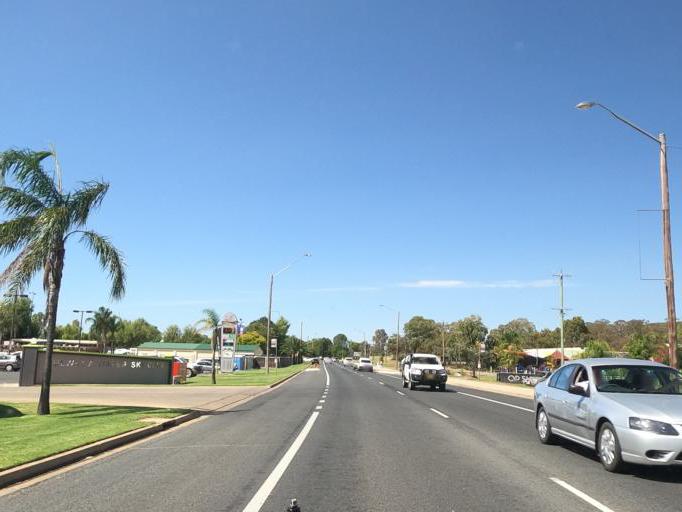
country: AU
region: New South Wales
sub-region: Corowa Shire
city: Mulwala
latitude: -35.9946
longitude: 146.0013
